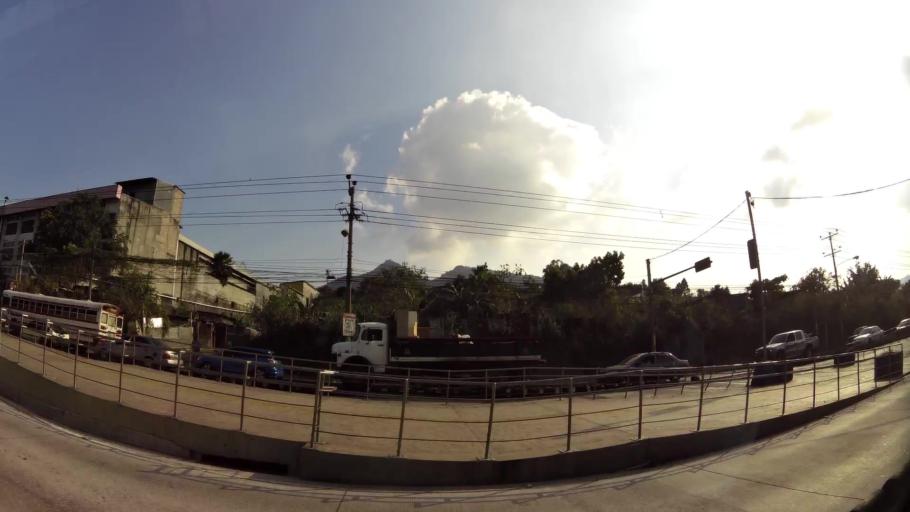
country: SV
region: San Salvador
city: Delgado
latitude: 13.7012
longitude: -89.1643
